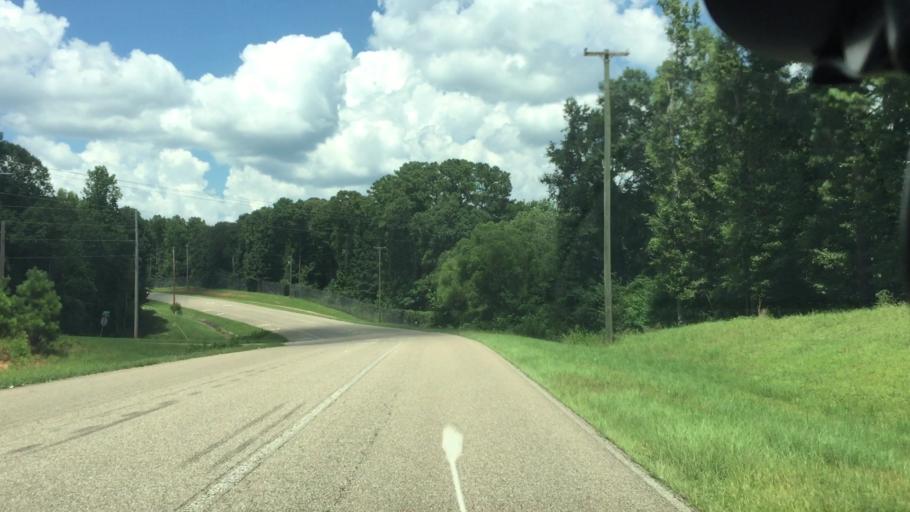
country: US
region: Alabama
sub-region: Pike County
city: Troy
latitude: 31.7746
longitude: -85.9787
